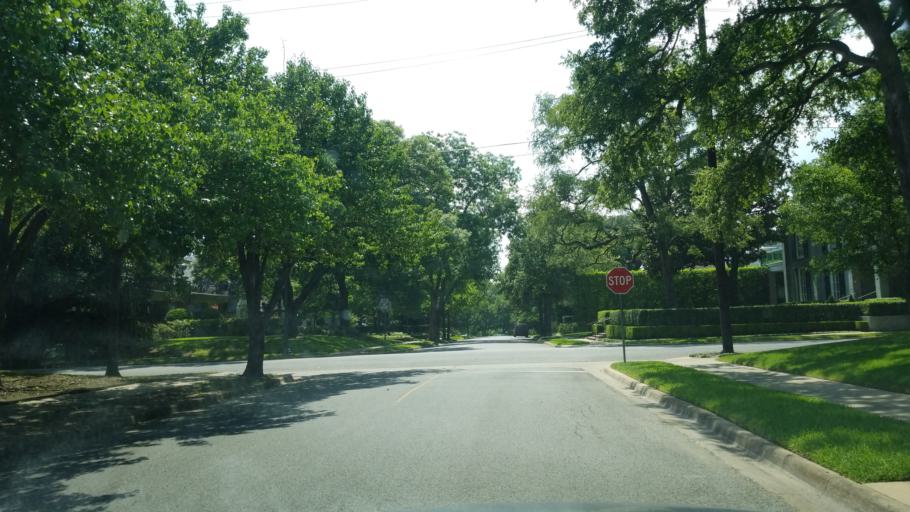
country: US
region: Texas
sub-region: Dallas County
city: Highland Park
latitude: 32.8309
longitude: -96.7998
